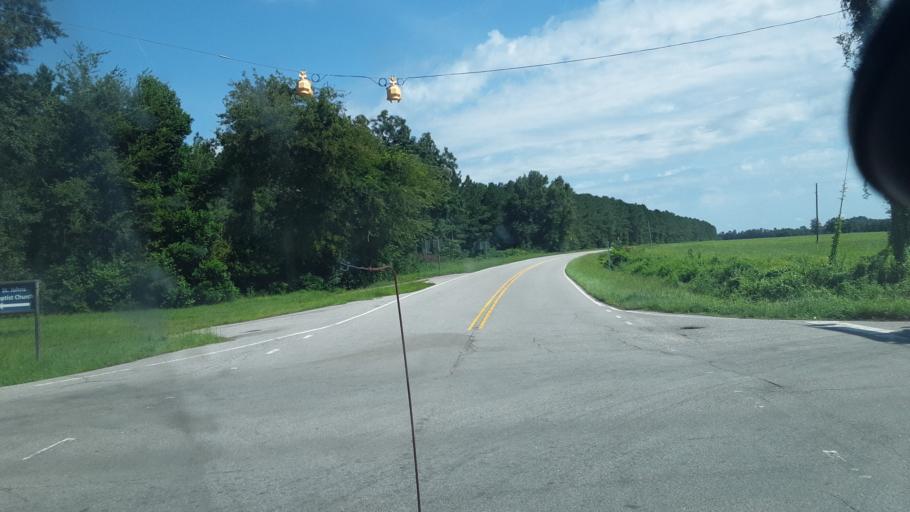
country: US
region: South Carolina
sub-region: Hampton County
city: Hampton
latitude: 33.0292
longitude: -81.0417
